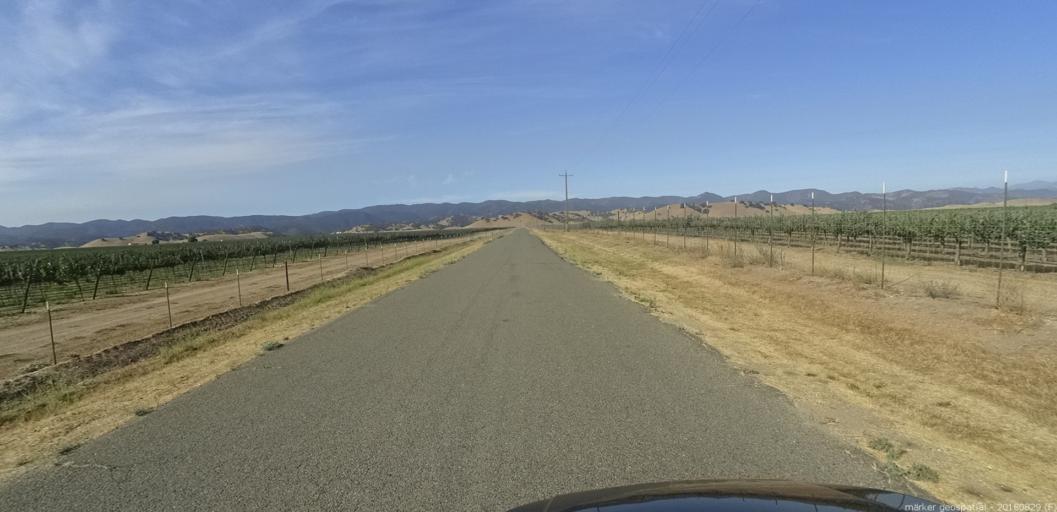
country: US
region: California
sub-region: Monterey County
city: King City
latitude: 36.0915
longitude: -121.0251
